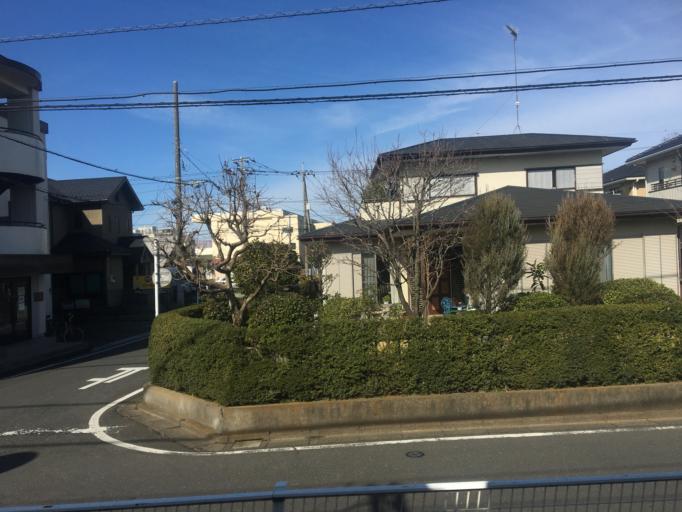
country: JP
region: Saitama
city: Sakado
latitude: 35.9741
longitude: 139.3979
